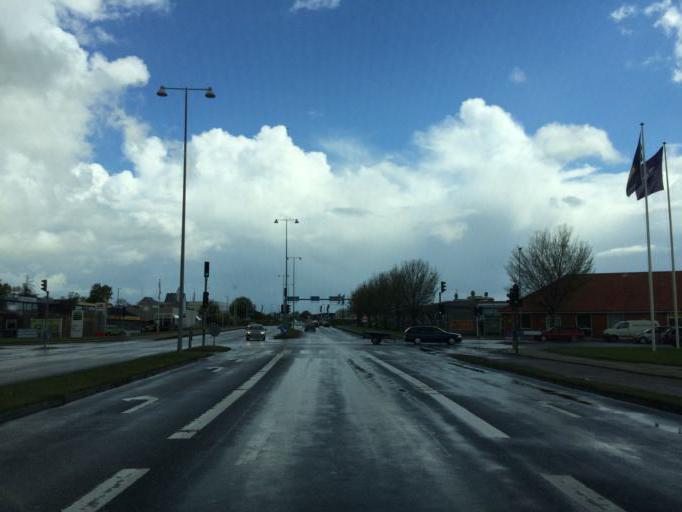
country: DK
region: Central Jutland
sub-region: Holstebro Kommune
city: Holstebro
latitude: 56.3758
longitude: 8.6142
